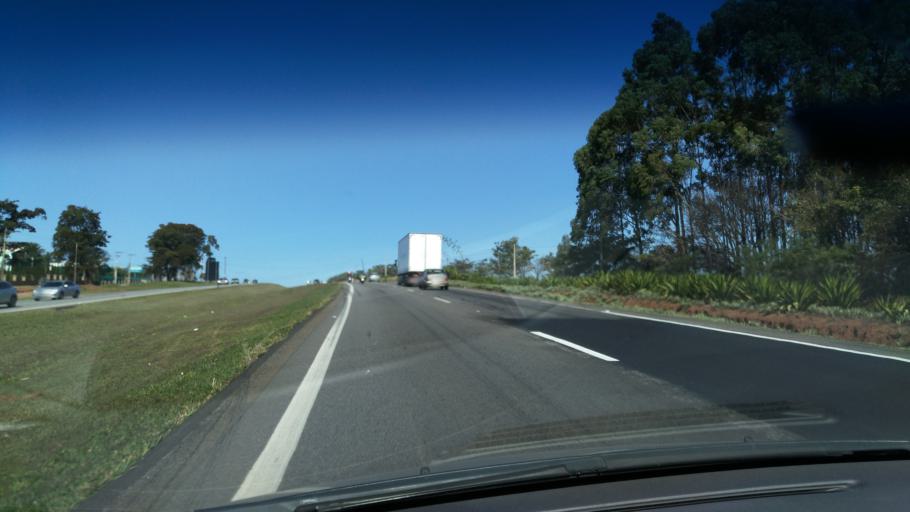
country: BR
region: Sao Paulo
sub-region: Jaguariuna
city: Jaguariuna
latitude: -22.6286
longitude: -47.0066
